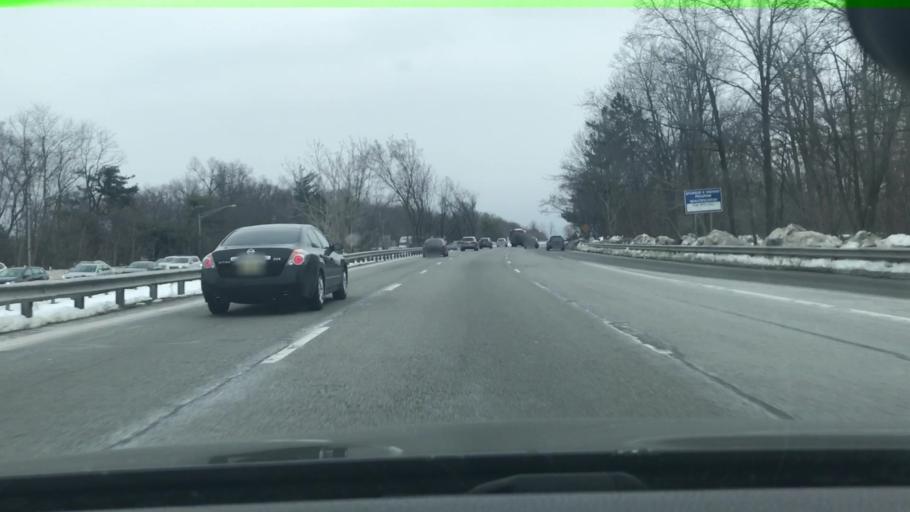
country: US
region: New Jersey
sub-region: Essex County
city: West Caldwell
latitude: 40.8238
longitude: -74.3194
